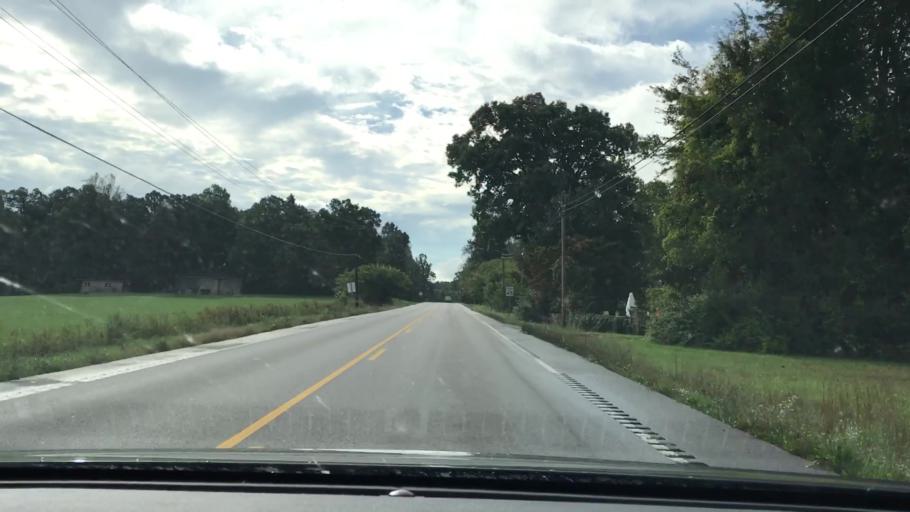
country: US
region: Tennessee
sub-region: Fentress County
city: Jamestown
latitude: 36.3790
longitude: -84.8758
